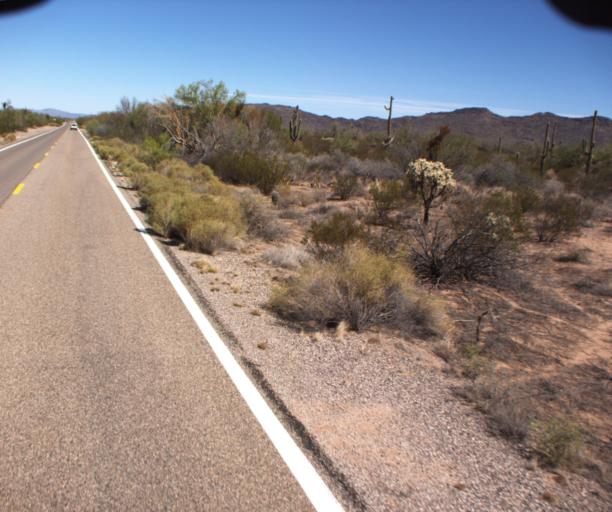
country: US
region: Arizona
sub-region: Pima County
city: Ajo
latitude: 32.1746
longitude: -112.7624
